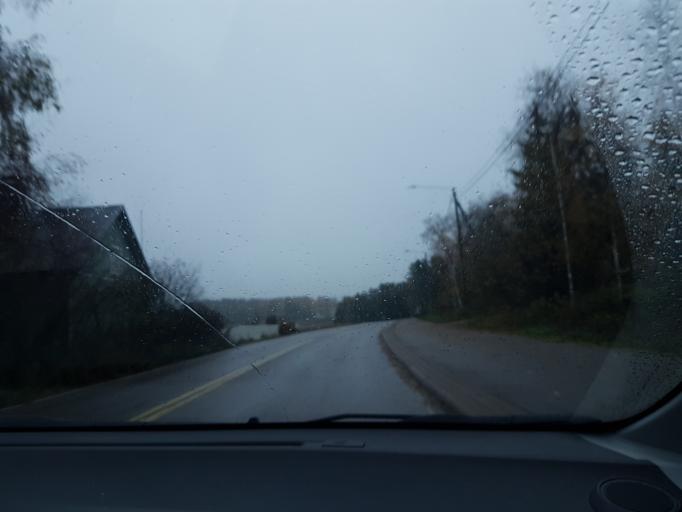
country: FI
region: Uusimaa
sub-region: Helsinki
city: Jaervenpaeae
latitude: 60.5744
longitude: 25.1517
